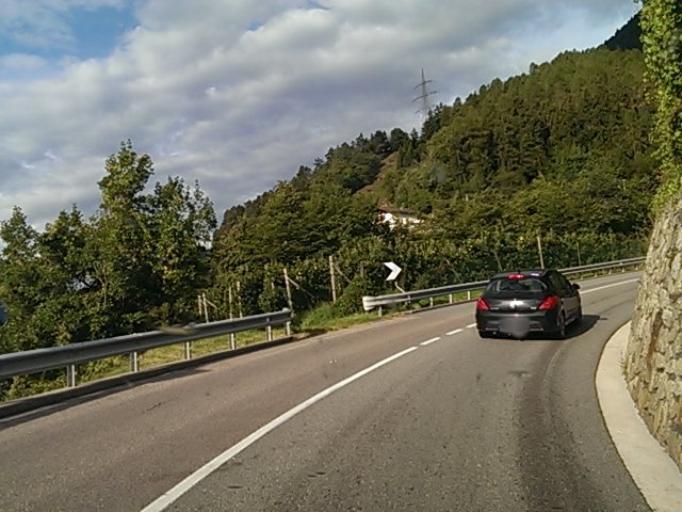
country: IT
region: Trentino-Alto Adige
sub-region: Bolzano
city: Cermes
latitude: 46.6099
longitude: 11.1198
